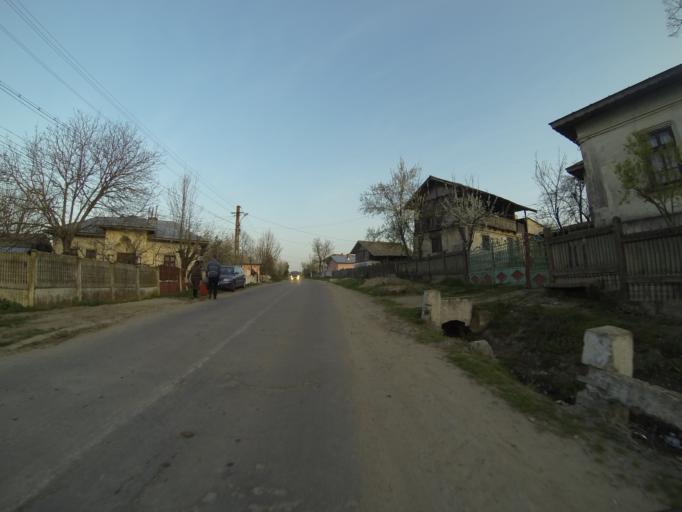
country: RO
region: Dolj
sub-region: Comuna Dranicu
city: Dranic
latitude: 44.0531
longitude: 23.8463
